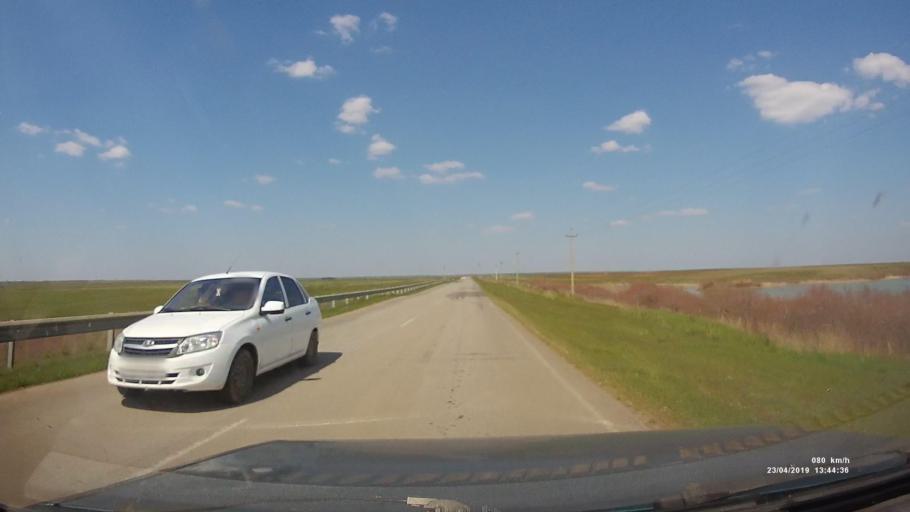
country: RU
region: Kalmykiya
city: Yashalta
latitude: 46.5828
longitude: 42.8171
